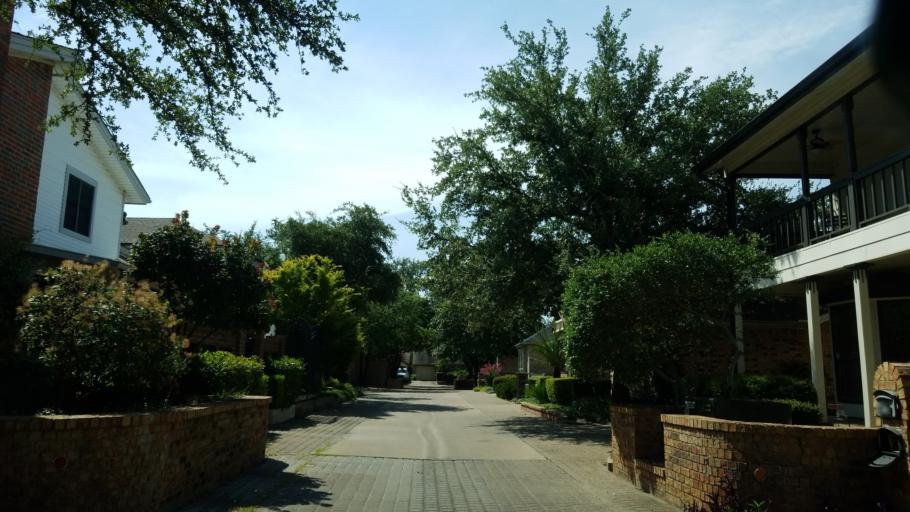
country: US
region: Texas
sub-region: Dallas County
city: Dallas
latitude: 32.7936
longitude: -96.7884
